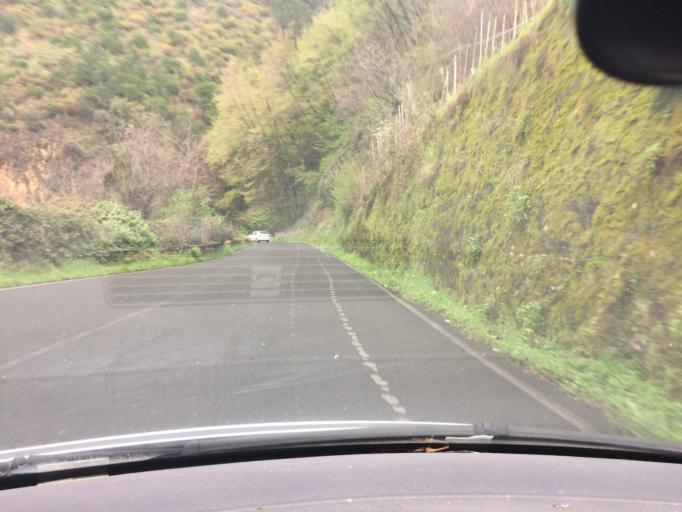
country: IT
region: Tuscany
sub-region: Provincia di Massa-Carrara
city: Massa
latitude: 44.0535
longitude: 10.1248
